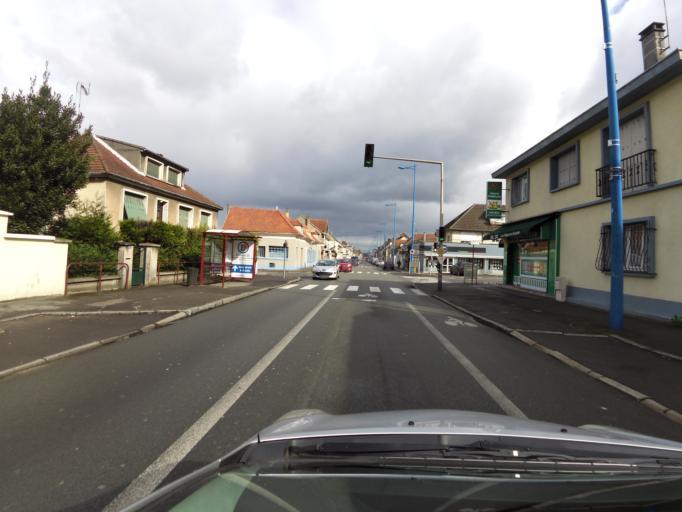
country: FR
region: Picardie
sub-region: Departement de l'Oise
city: Pont-Sainte-Maxence
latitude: 49.2963
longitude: 2.6047
